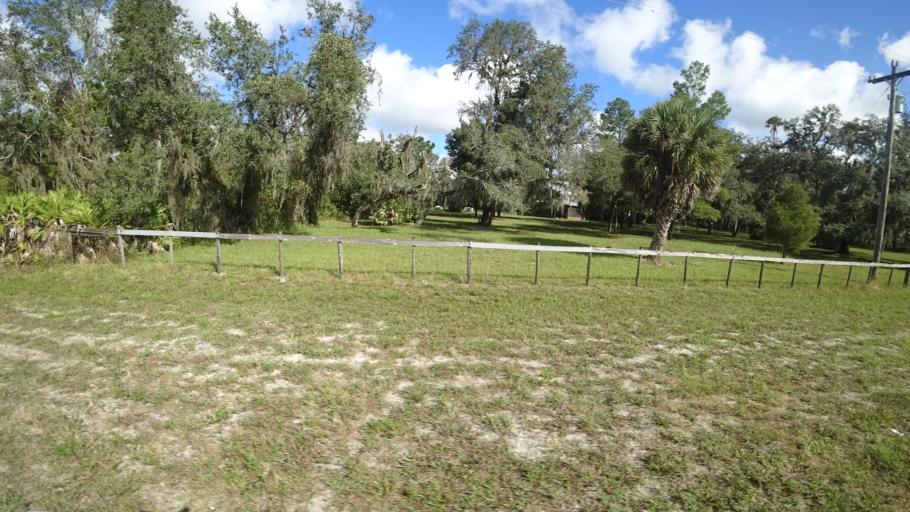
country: US
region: Florida
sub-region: Sarasota County
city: Lake Sarasota
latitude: 27.3392
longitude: -82.1876
